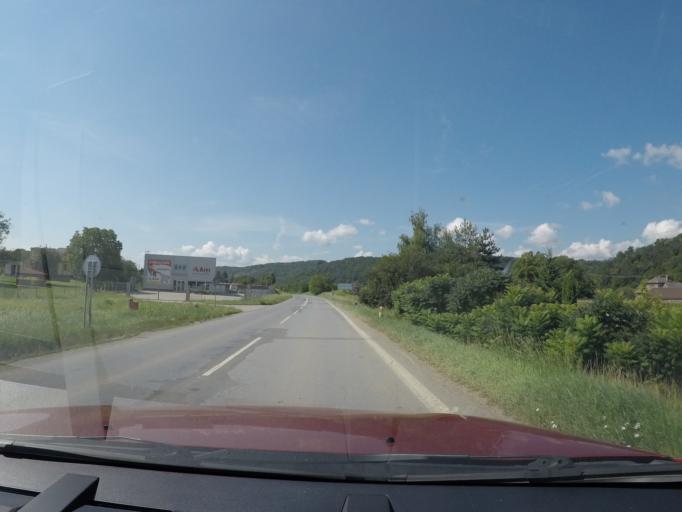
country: SK
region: Presovsky
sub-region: Okres Presov
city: Presov
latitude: 48.9613
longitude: 21.2429
